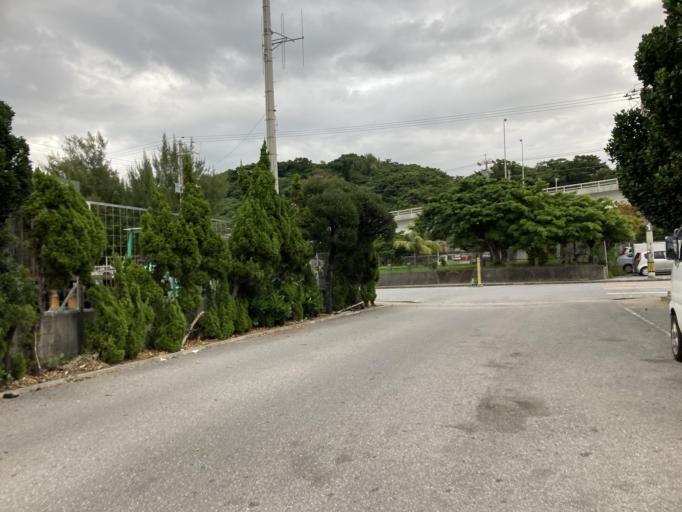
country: JP
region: Okinawa
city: Naha-shi
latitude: 26.2301
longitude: 127.6807
